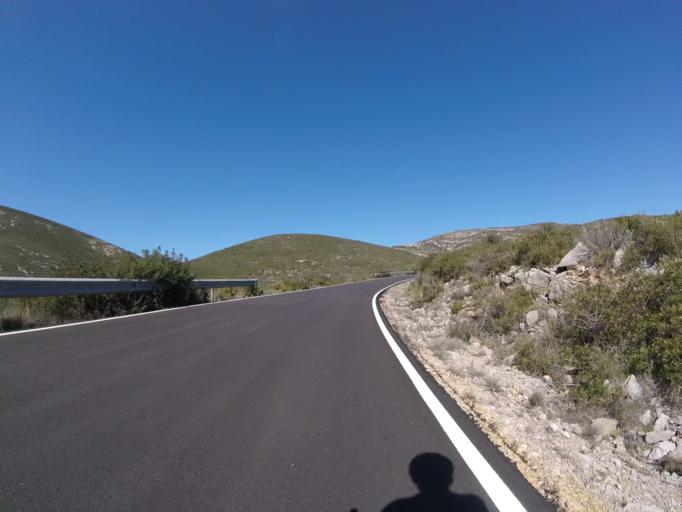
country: ES
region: Valencia
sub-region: Provincia de Castello
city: Cervera del Maestre
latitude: 40.4031
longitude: 0.2279
